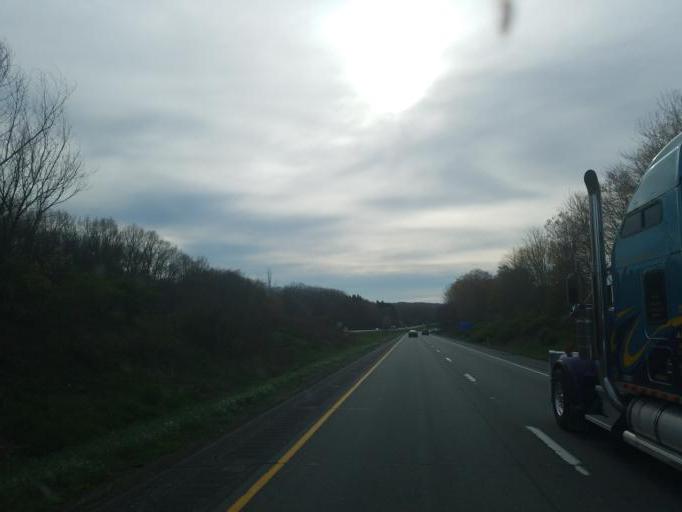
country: US
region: Pennsylvania
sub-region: Mercer County
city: Mercer
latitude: 41.1940
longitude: -80.2140
